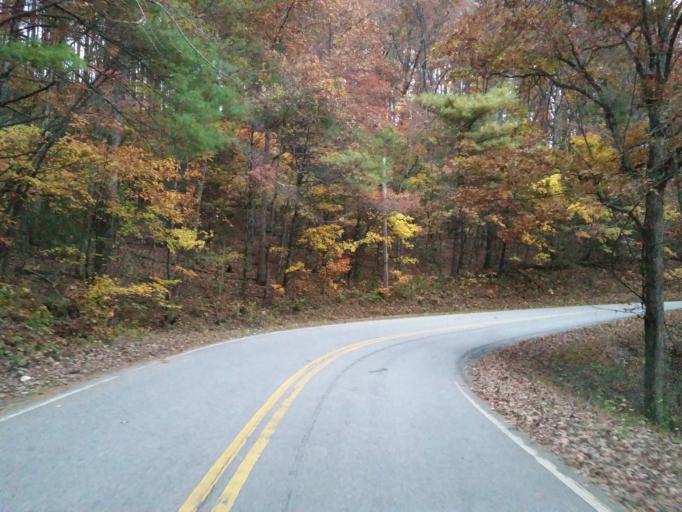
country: US
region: Georgia
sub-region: Lumpkin County
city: Dahlonega
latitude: 34.7056
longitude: -84.0651
